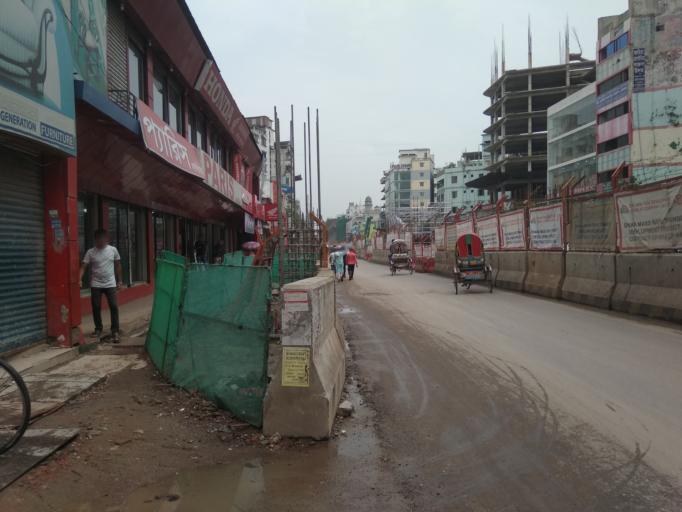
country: BD
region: Dhaka
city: Azimpur
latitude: 23.8000
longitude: 90.3718
